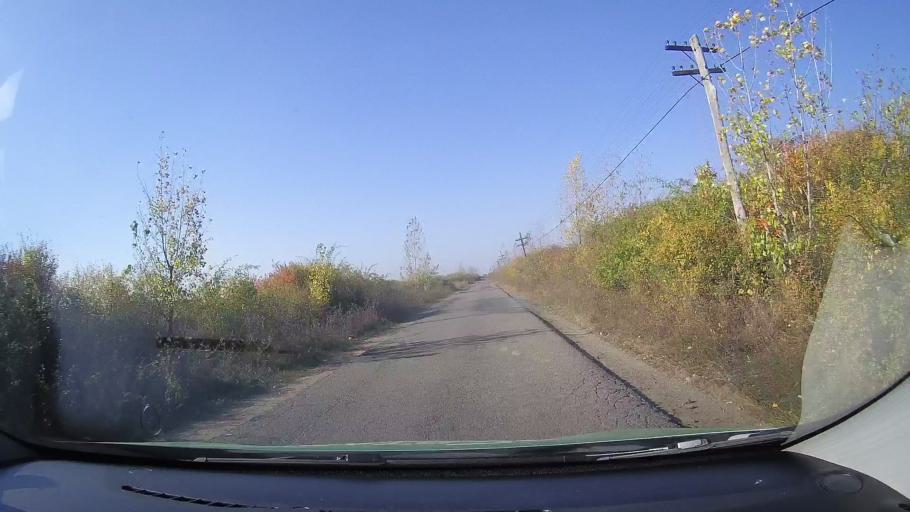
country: RO
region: Satu Mare
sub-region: Comuna Sauca
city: Sauca
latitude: 47.4692
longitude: 22.5119
